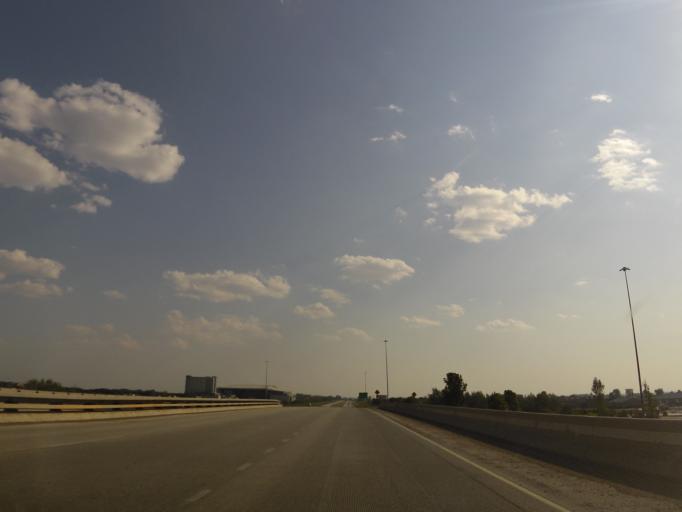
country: US
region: North Dakota
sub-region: Grand Forks County
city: Grand Forks
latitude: 47.9187
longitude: -97.0938
